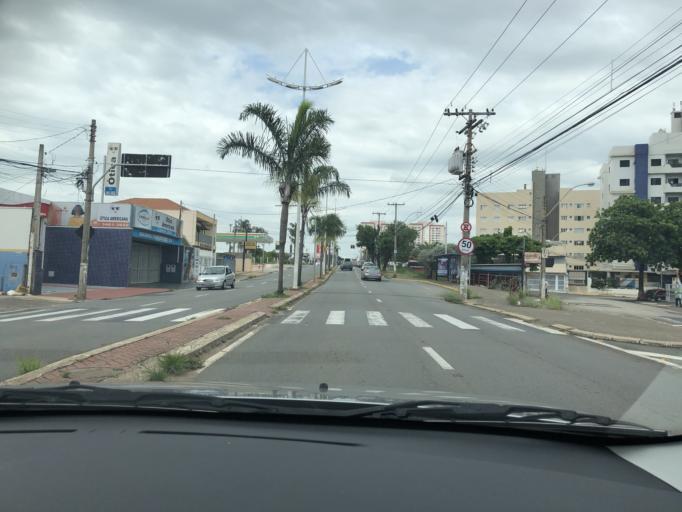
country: BR
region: Sao Paulo
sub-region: Americana
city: Americana
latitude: -22.7592
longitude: -47.3390
